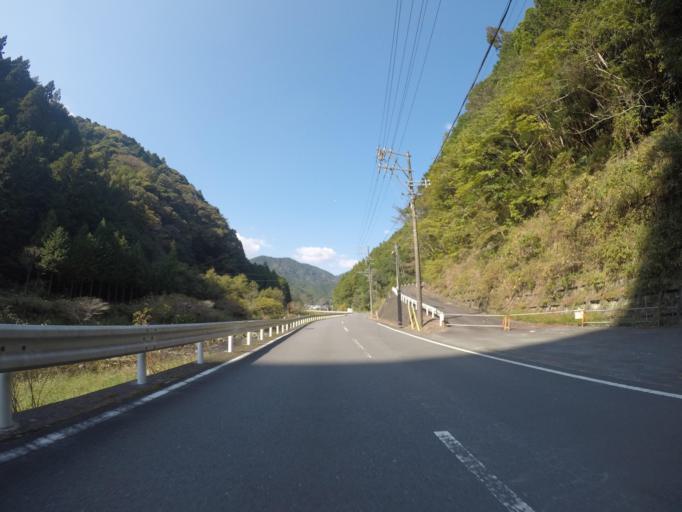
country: JP
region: Shizuoka
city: Fujinomiya
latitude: 35.1143
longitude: 138.4863
